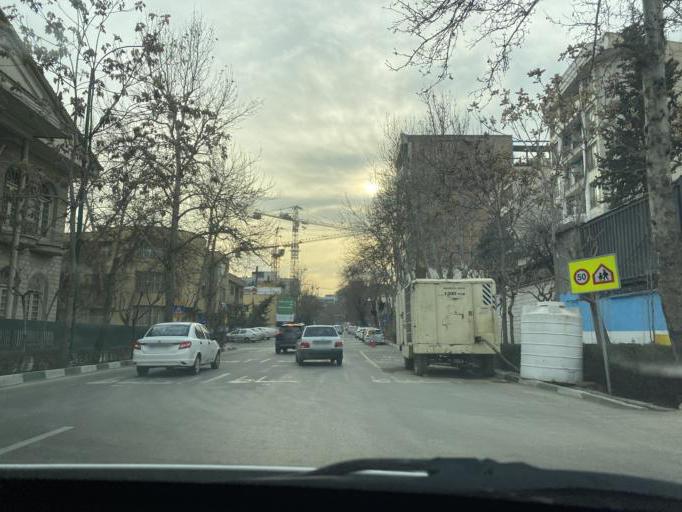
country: IR
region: Tehran
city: Tajrish
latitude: 35.8093
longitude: 51.4434
